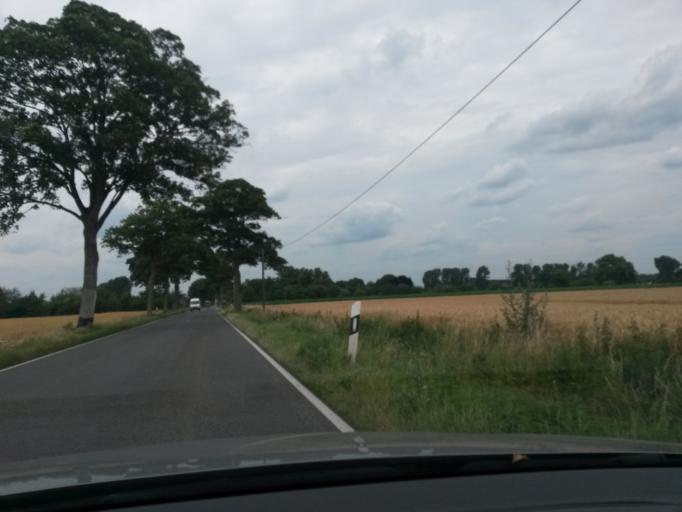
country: DE
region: North Rhine-Westphalia
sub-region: Regierungsbezirk Dusseldorf
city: Viersen
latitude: 51.3013
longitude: 6.3882
